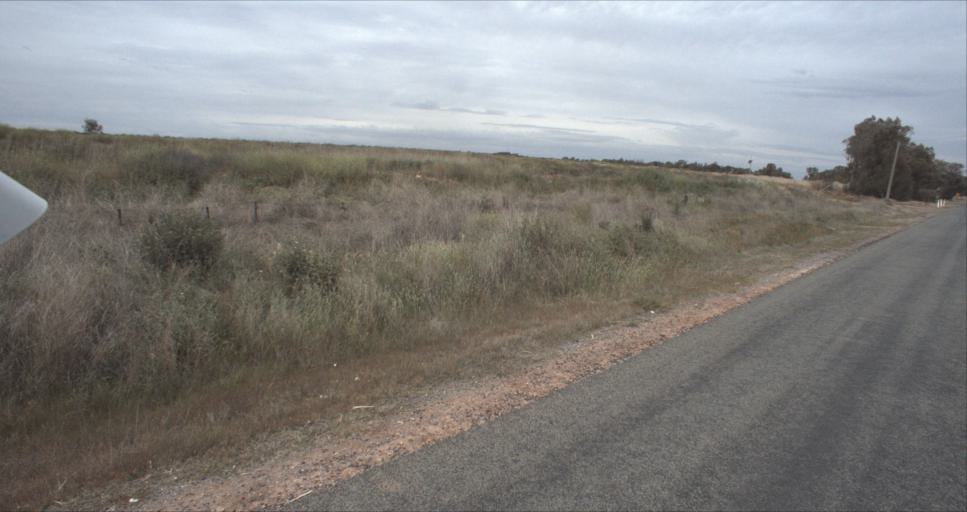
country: AU
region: New South Wales
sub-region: Leeton
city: Leeton
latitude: -34.4393
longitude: 146.3760
